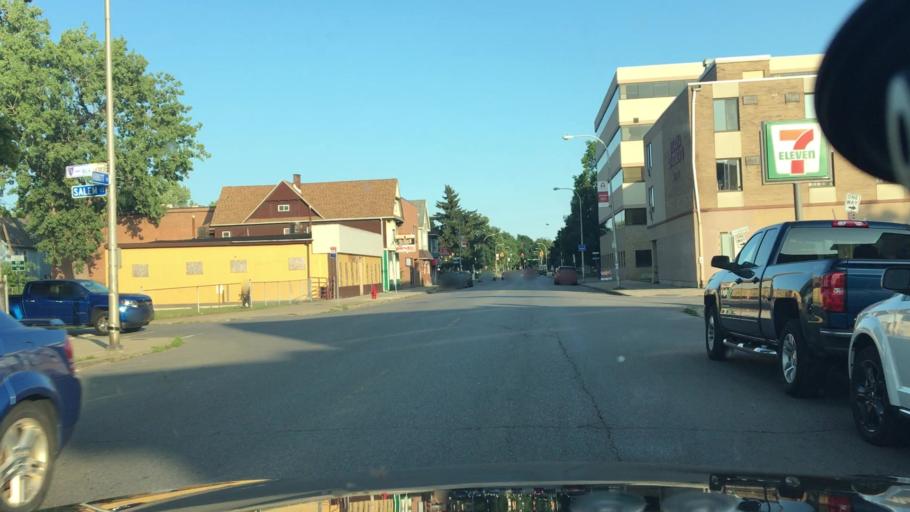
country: US
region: New York
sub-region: Erie County
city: West Seneca
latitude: 42.8498
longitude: -78.8146
